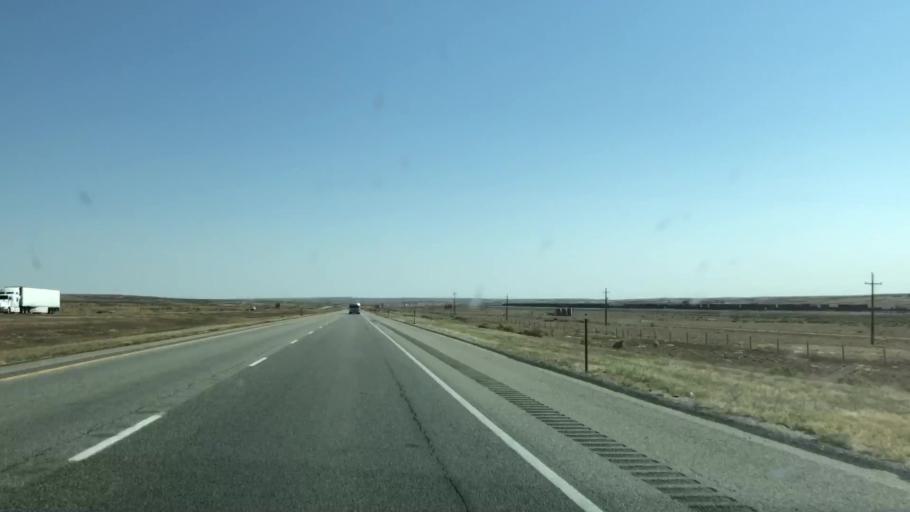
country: US
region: Wyoming
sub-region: Carbon County
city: Rawlins
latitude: 41.6798
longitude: -107.9684
